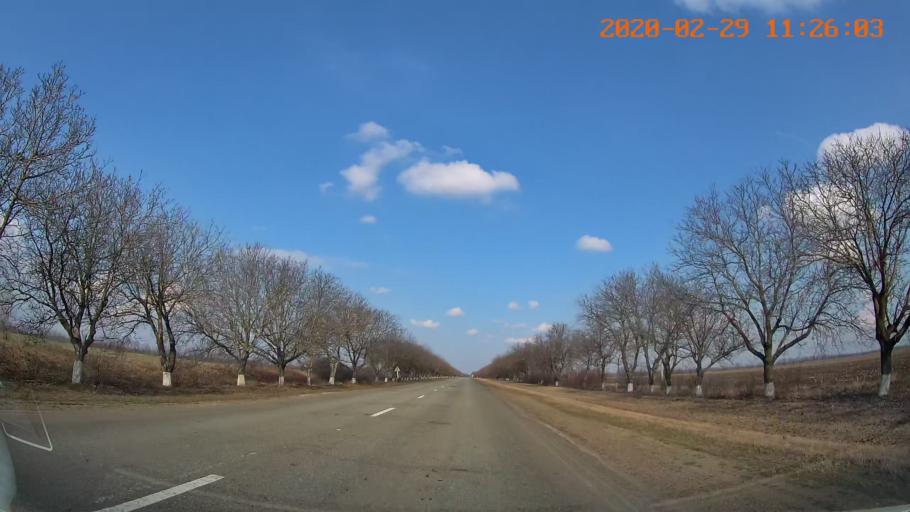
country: MD
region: Telenesti
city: Cocieri
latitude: 47.4475
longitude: 29.1477
